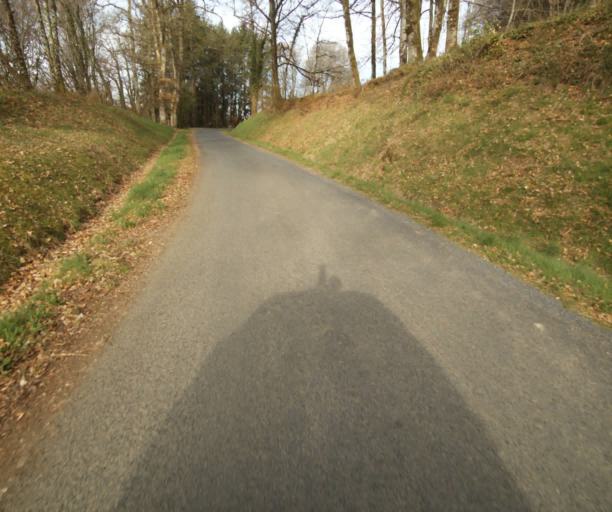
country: FR
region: Limousin
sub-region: Departement de la Correze
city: Chamboulive
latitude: 45.4464
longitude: 1.7575
